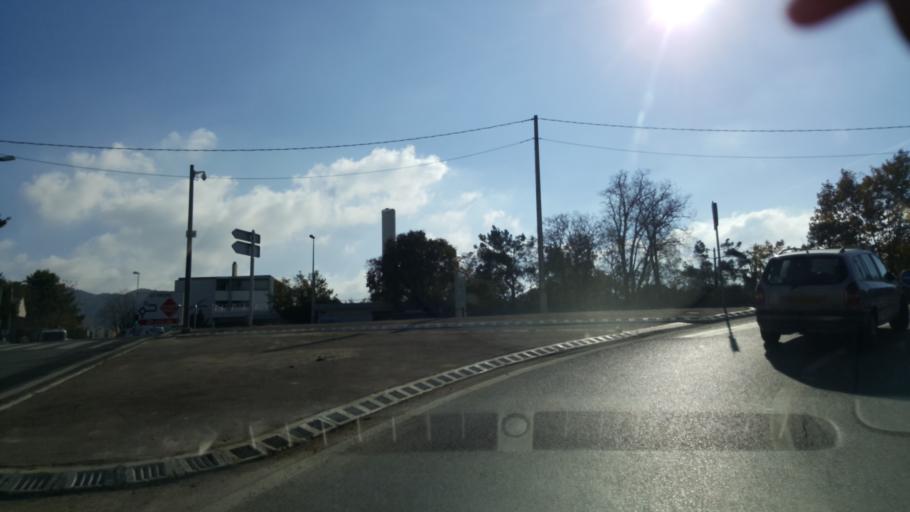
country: FR
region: Provence-Alpes-Cote d'Azur
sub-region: Departement des Bouches-du-Rhone
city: Marseille 10
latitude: 43.2752
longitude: 5.4263
